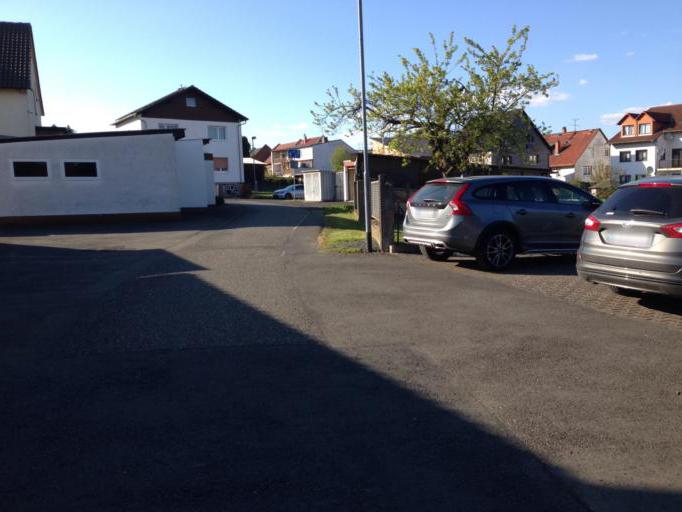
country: DE
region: Hesse
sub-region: Regierungsbezirk Giessen
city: Lich
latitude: 50.5493
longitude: 8.7778
